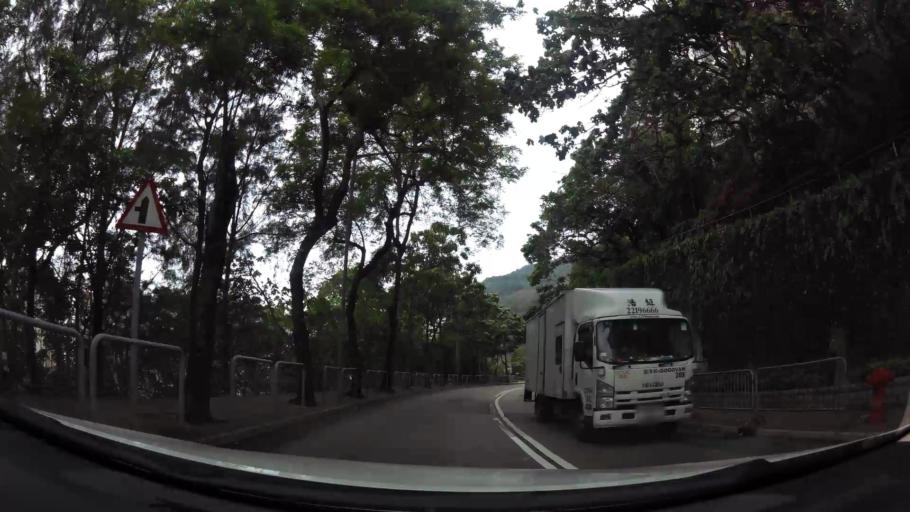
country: HK
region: Central and Western
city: Central
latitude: 22.2694
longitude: 114.1257
